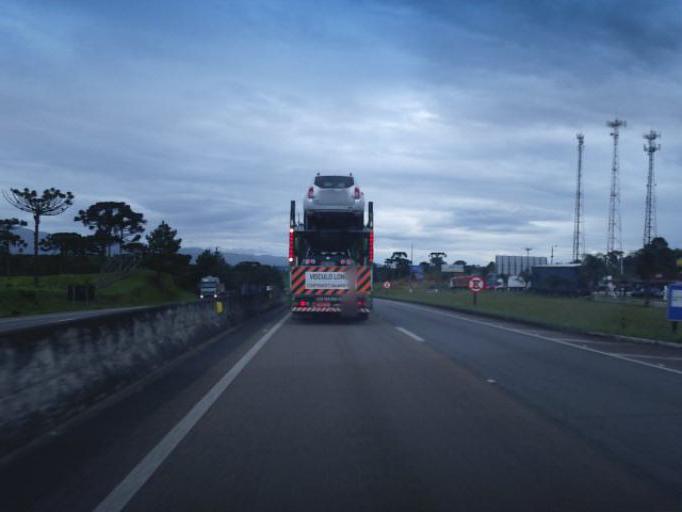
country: BR
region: Parana
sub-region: Sao Jose Dos Pinhais
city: Sao Jose dos Pinhais
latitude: -25.8357
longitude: -49.1089
